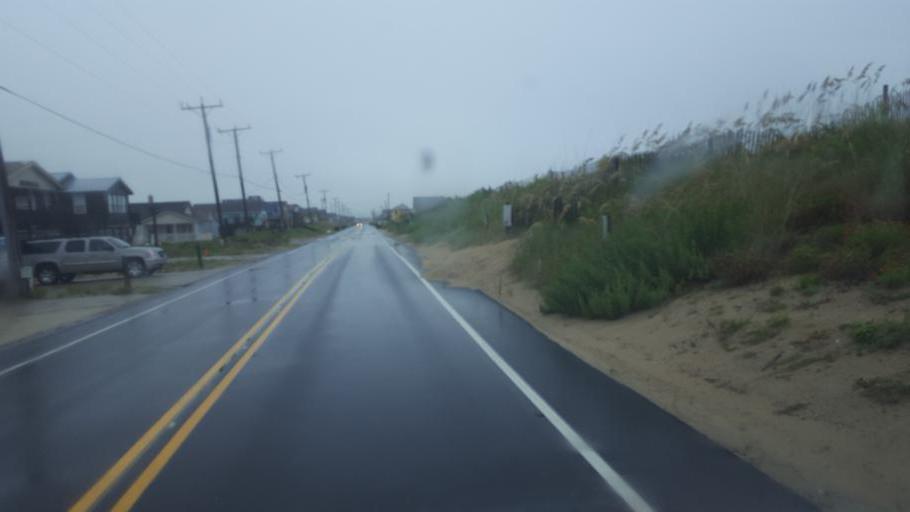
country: US
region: North Carolina
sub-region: Dare County
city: Kitty Hawk
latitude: 36.0722
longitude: -75.6940
